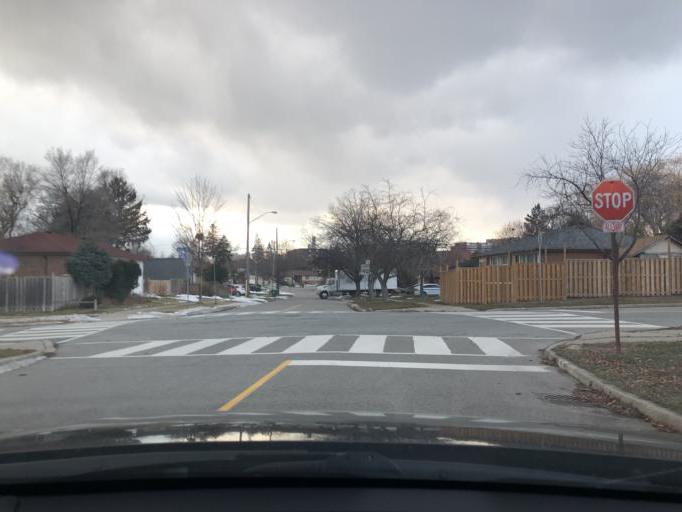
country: CA
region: Ontario
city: Scarborough
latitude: 43.7800
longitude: -79.2924
